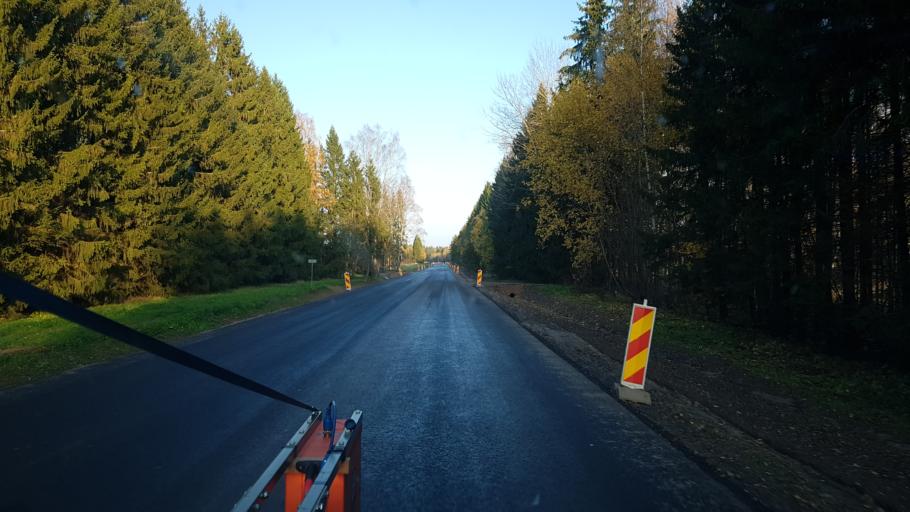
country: EE
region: Polvamaa
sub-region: Polva linn
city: Polva
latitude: 57.9481
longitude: 27.2264
